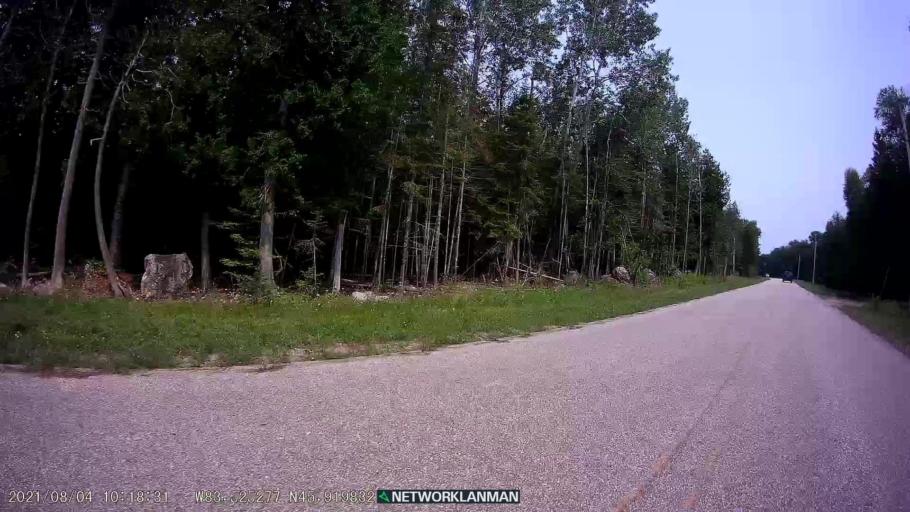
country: CA
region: Ontario
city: Thessalon
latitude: 45.9192
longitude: -83.5261
